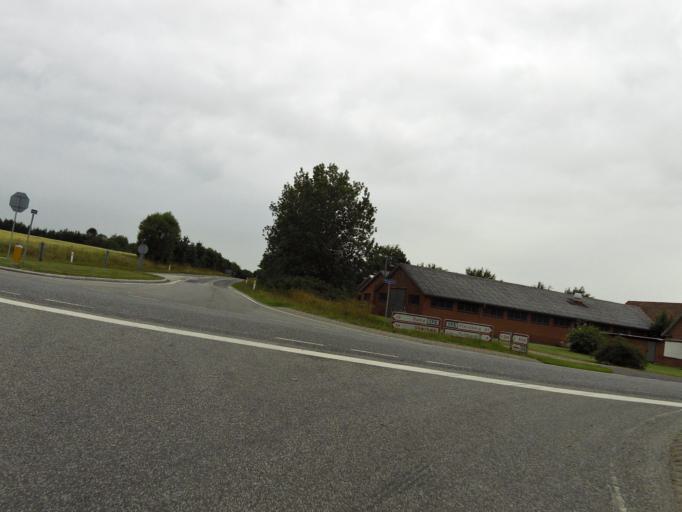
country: DK
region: South Denmark
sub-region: Tonder Kommune
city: Toftlund
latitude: 55.1685
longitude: 8.9649
